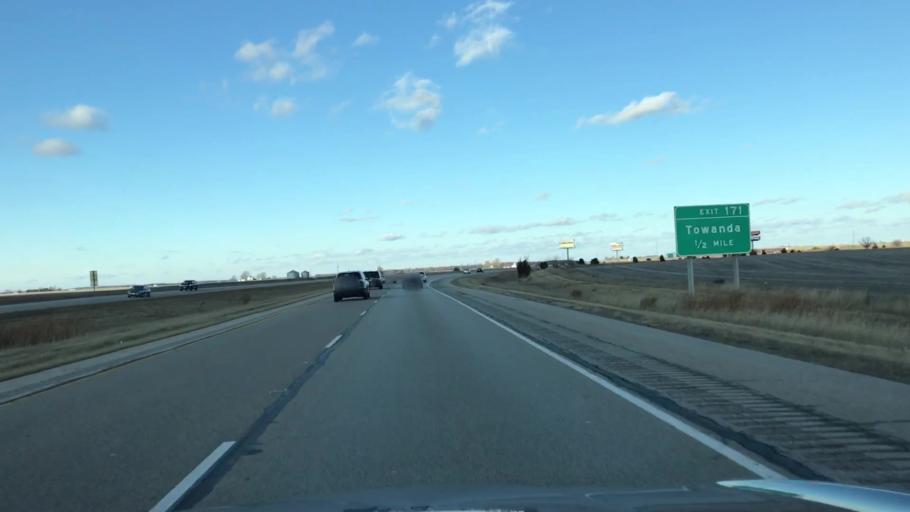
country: US
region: Illinois
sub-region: McLean County
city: Hudson
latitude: 40.5628
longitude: -88.9083
